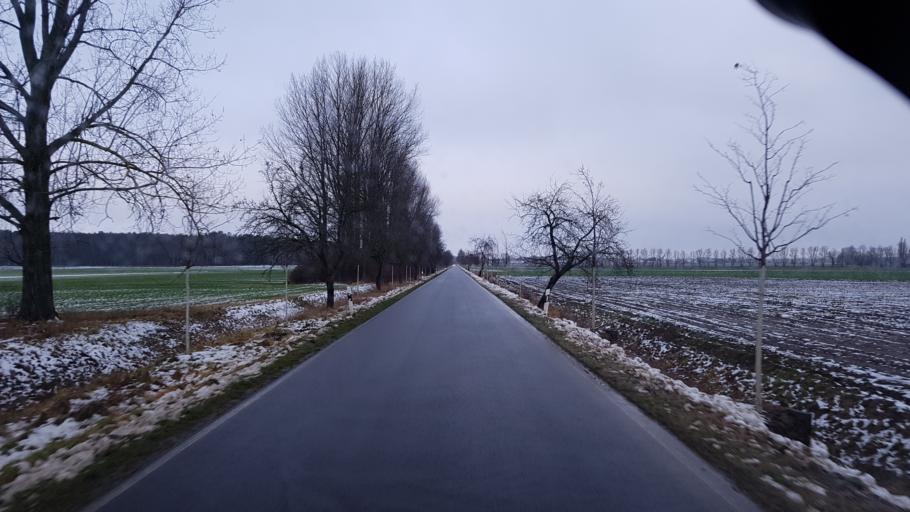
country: DE
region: Brandenburg
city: Luckau
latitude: 51.8079
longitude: 13.7172
